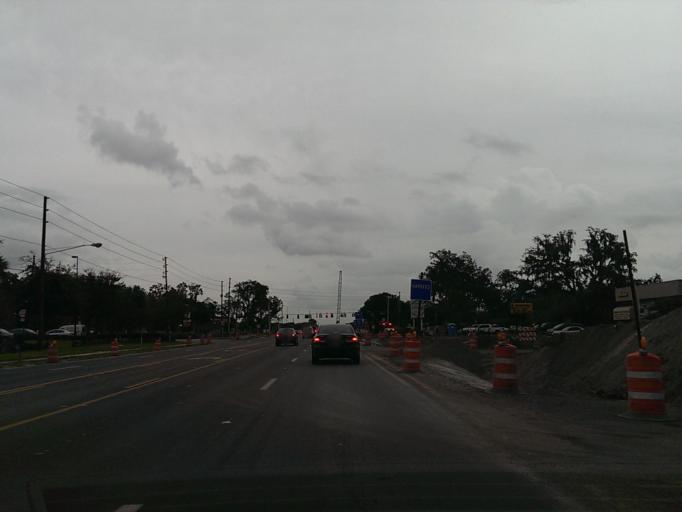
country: US
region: Florida
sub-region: Orange County
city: Ocoee
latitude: 28.5517
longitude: -81.5402
